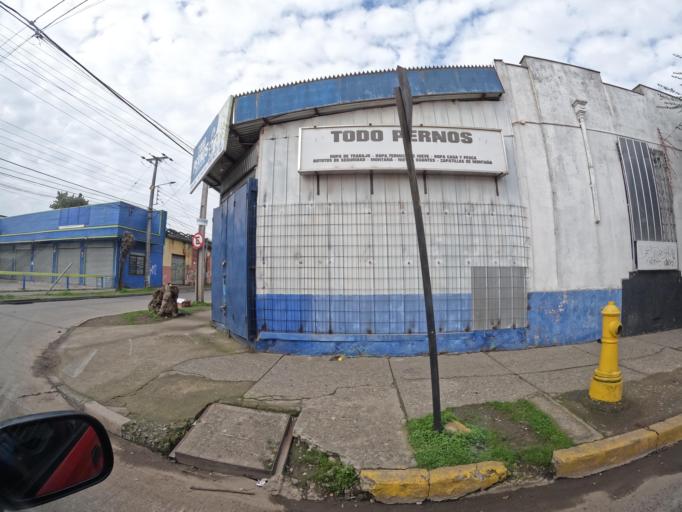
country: CL
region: Maule
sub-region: Provincia de Linares
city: Linares
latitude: -35.8500
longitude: -71.5925
